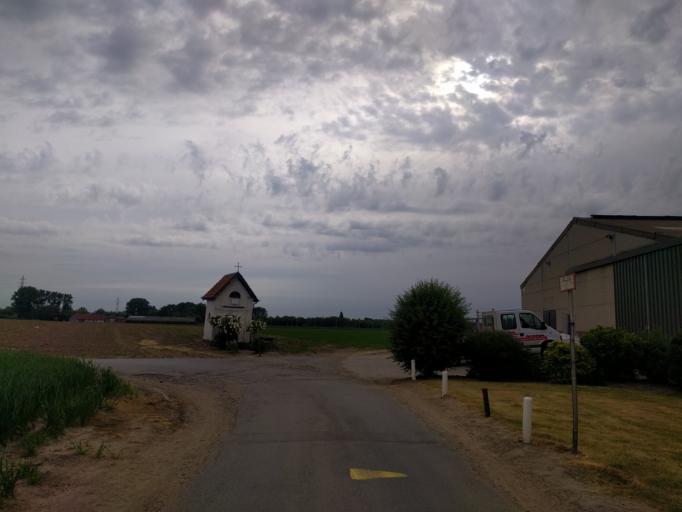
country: BE
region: Flanders
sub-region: Provincie West-Vlaanderen
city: Wevelgem
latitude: 50.8305
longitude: 3.1760
